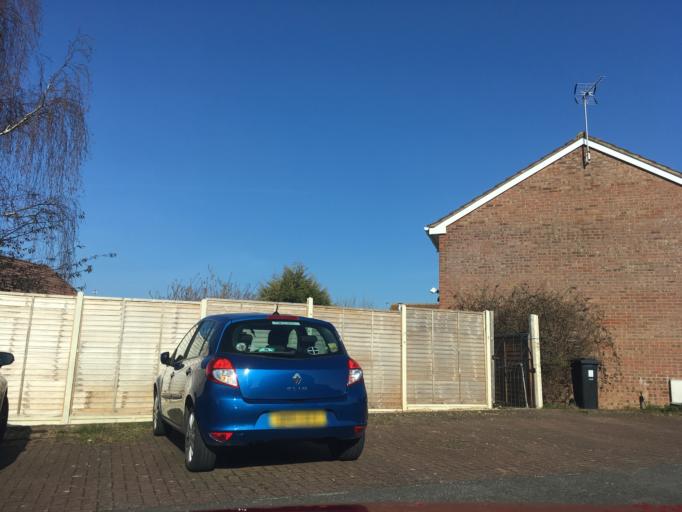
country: GB
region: England
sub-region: South Gloucestershire
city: Yate
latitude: 51.5428
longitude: -2.4203
